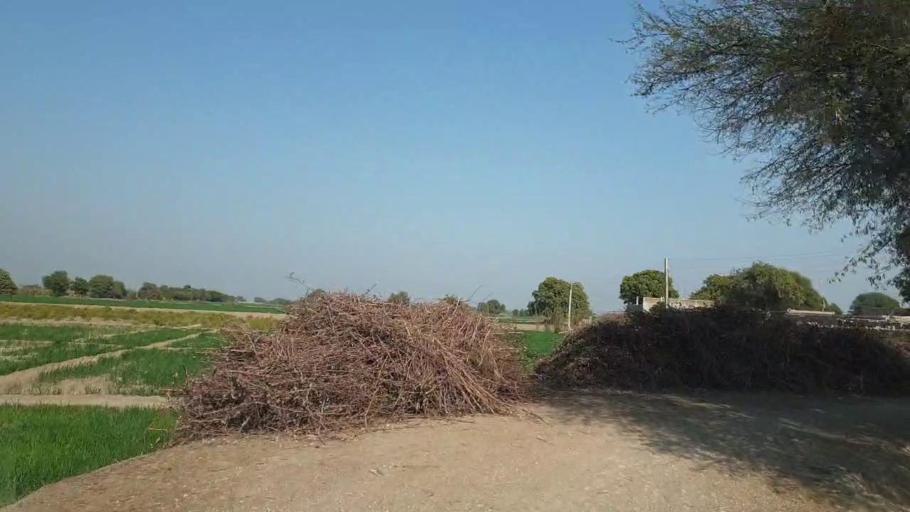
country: PK
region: Sindh
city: Tando Jam
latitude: 25.5051
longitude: 68.4962
